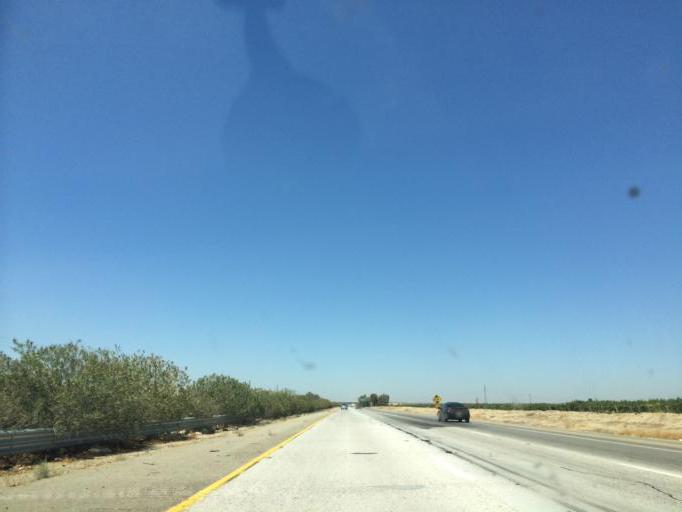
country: US
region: California
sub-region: Kern County
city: Weedpatch
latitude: 35.1138
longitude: -118.9855
